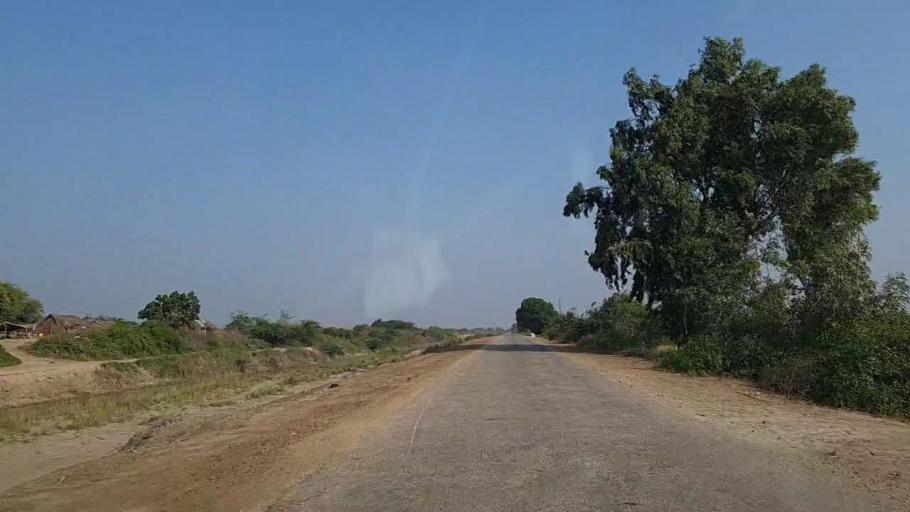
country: PK
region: Sindh
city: Mirpur Sakro
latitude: 24.6310
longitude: 67.6326
